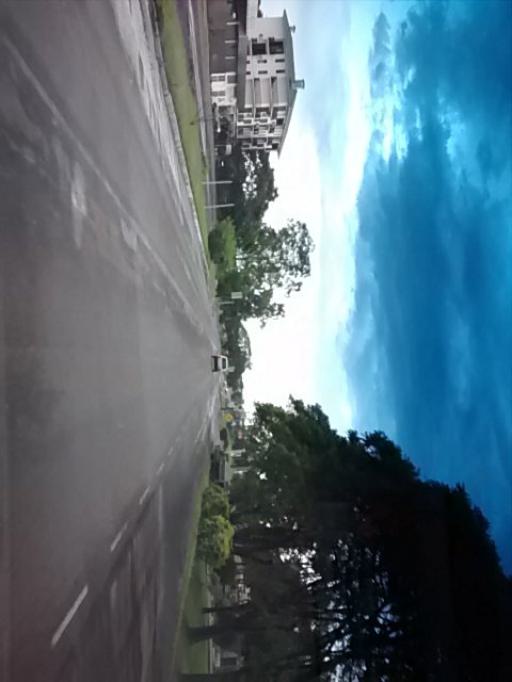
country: BR
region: Rio Grande do Sul
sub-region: Santa Maria
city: Santa Maria
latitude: -29.7191
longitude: -53.8082
